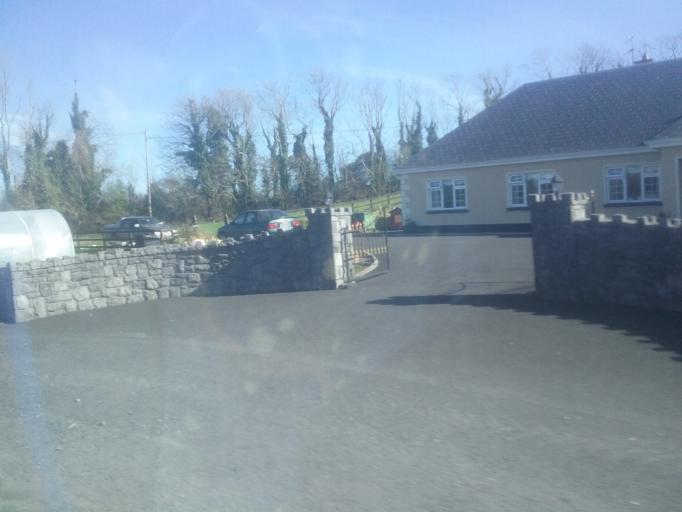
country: IE
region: Munster
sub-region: An Clar
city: Ennis
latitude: 52.9506
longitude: -9.0497
